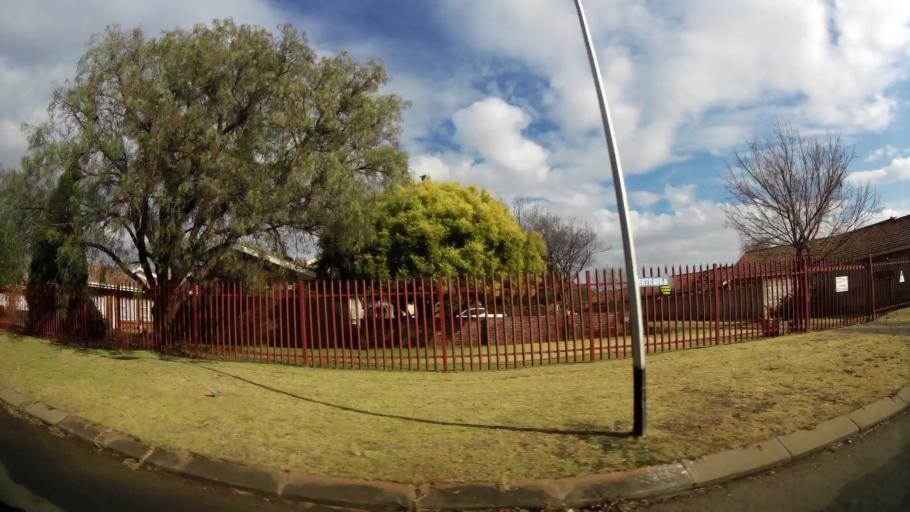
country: ZA
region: Gauteng
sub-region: Sedibeng District Municipality
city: Meyerton
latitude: -26.5523
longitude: 28.0353
